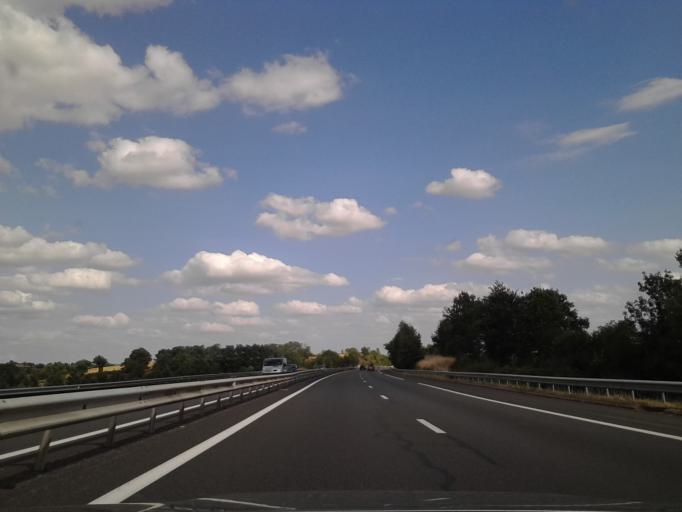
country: FR
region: Auvergne
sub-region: Departement de l'Allier
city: Doyet
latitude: 46.3475
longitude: 2.8639
